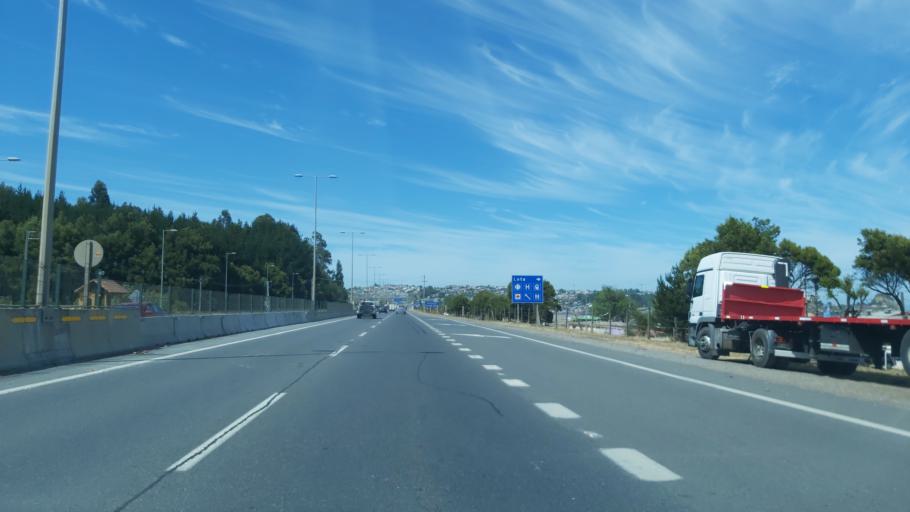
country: CL
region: Biobio
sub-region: Provincia de Concepcion
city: Coronel
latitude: -37.0635
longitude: -73.1418
